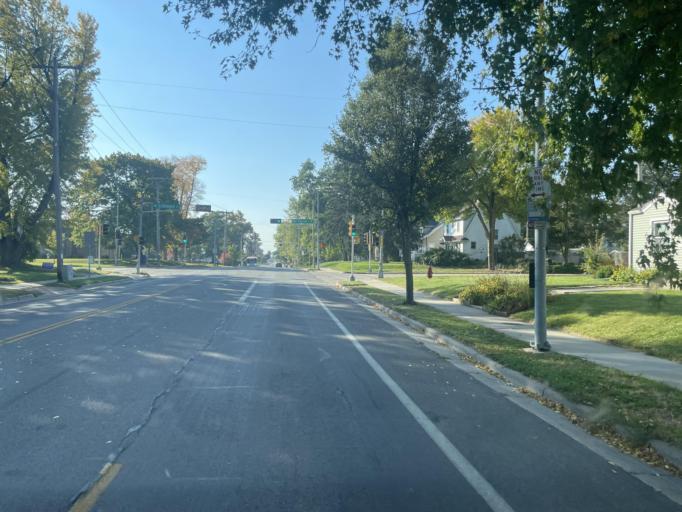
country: US
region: Wisconsin
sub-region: Dane County
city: Maple Bluff
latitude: 43.1194
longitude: -89.3638
